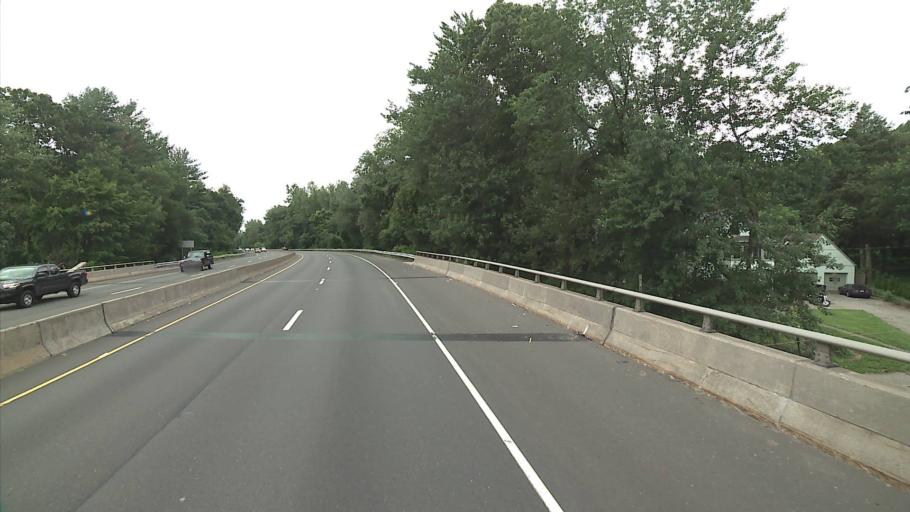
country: US
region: Connecticut
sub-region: New Haven County
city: Ansonia
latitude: 41.3514
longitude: -73.0953
